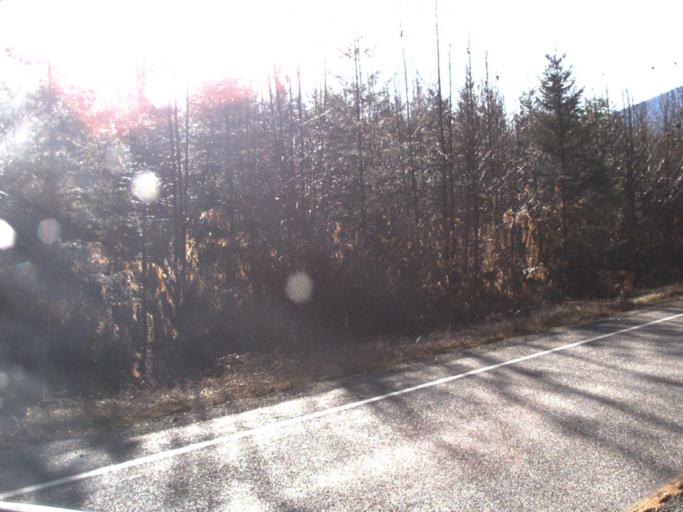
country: US
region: Washington
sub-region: Snohomish County
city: Darrington
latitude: 48.3877
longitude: -121.5515
